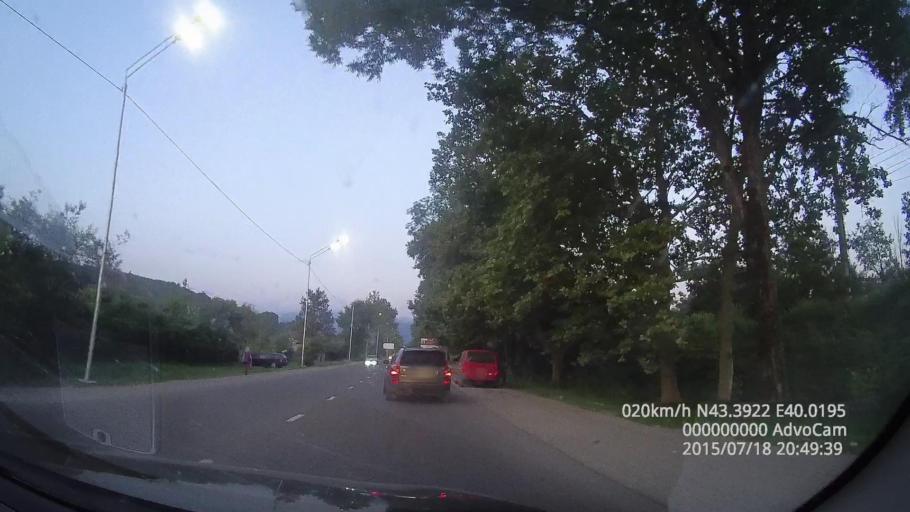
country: GE
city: Gantiadi
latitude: 43.3921
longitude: 40.0202
